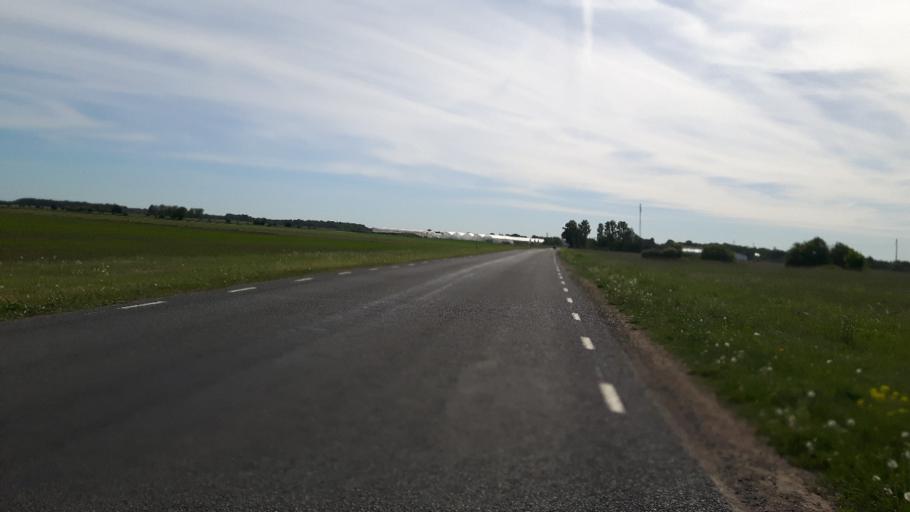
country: EE
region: Harju
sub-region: Raasiku vald
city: Arukula
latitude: 59.4331
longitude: 25.1183
